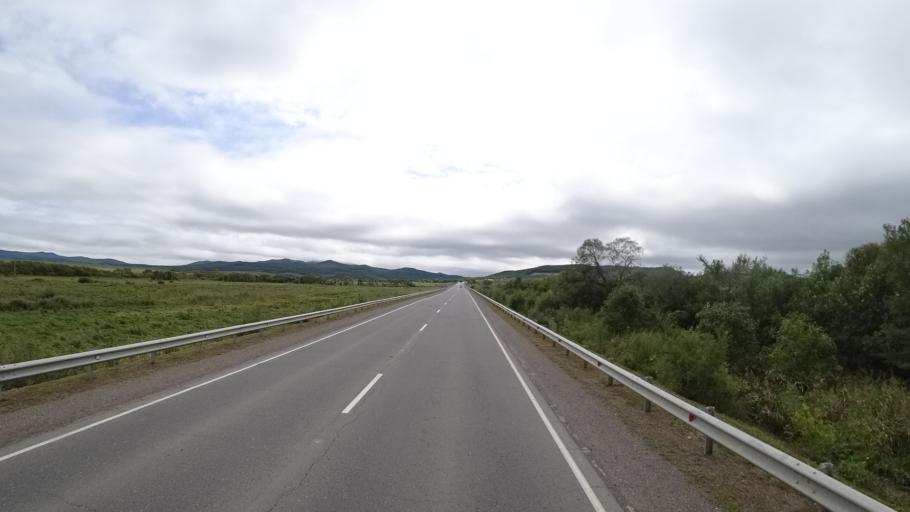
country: RU
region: Primorskiy
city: Monastyrishche
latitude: 44.1790
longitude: 132.4414
